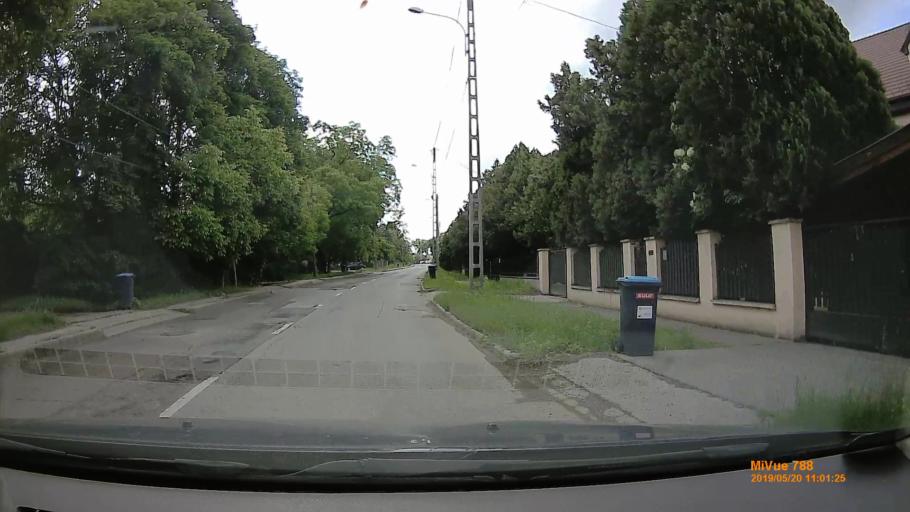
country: HU
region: Budapest
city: Budapest XVII. keruelet
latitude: 47.4810
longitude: 19.2914
